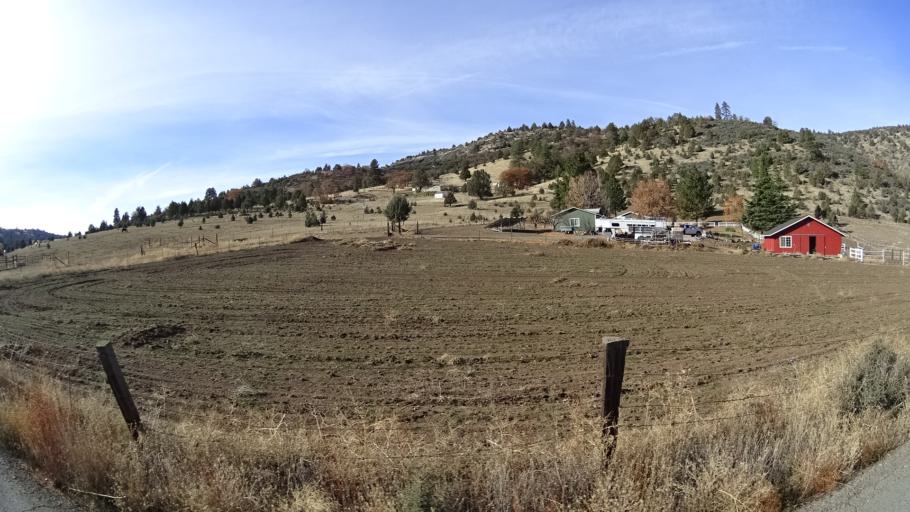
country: US
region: California
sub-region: Siskiyou County
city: Montague
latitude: 41.5973
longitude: -122.5767
